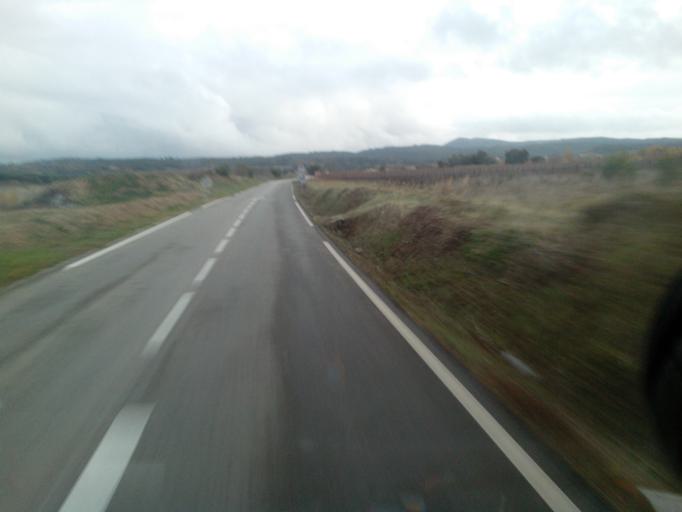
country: FR
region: Languedoc-Roussillon
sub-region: Departement de l'Herault
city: Saint-Jean-de-Fos
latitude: 43.7022
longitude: 3.5659
